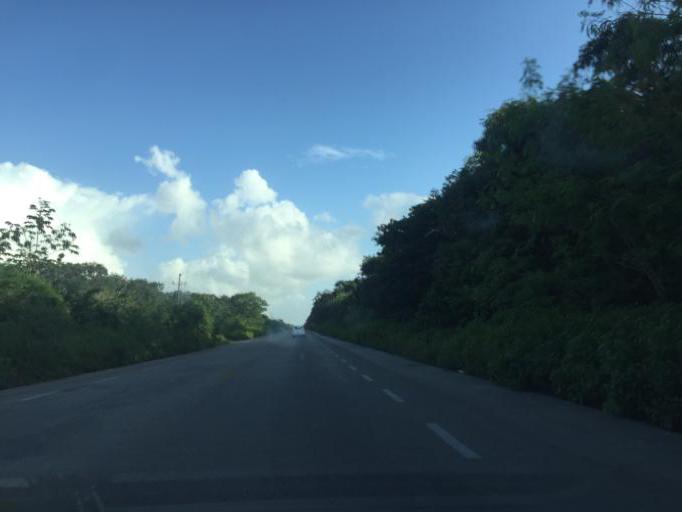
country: MX
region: Quintana Roo
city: Coba
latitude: 20.4977
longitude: -87.7095
